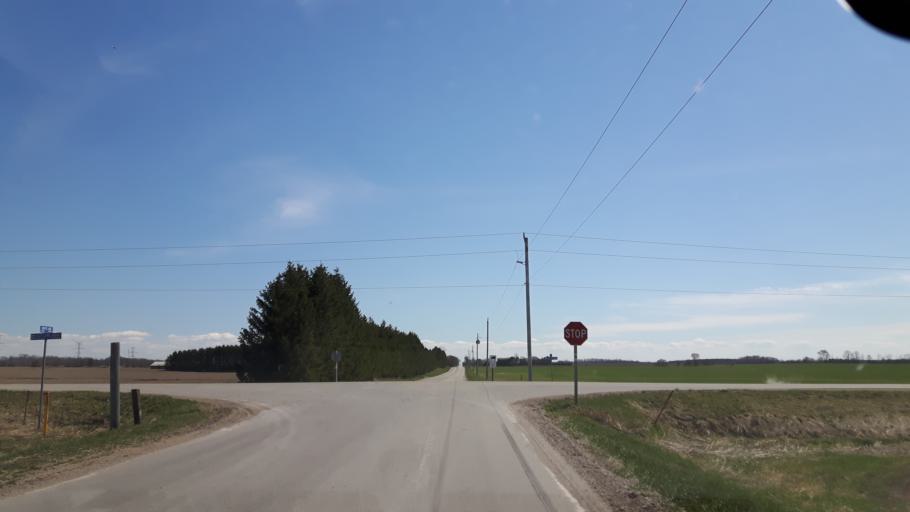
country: CA
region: Ontario
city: Goderich
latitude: 43.6431
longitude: -81.6440
